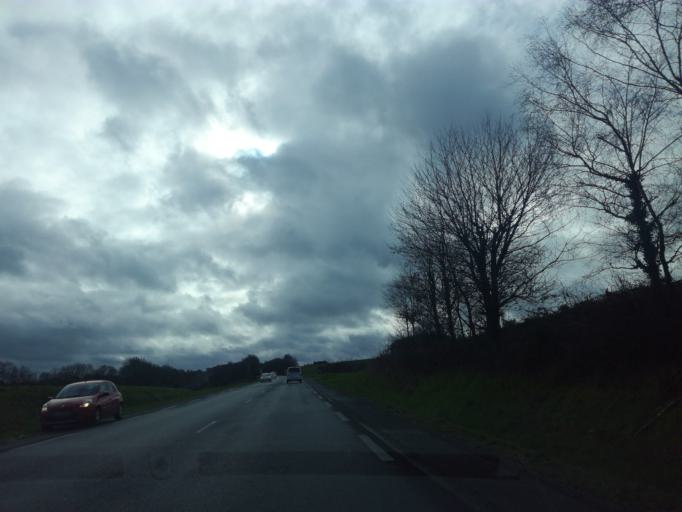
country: FR
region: Brittany
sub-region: Departement du Morbihan
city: Saint-Thuriau
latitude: 48.0042
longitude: -2.9785
